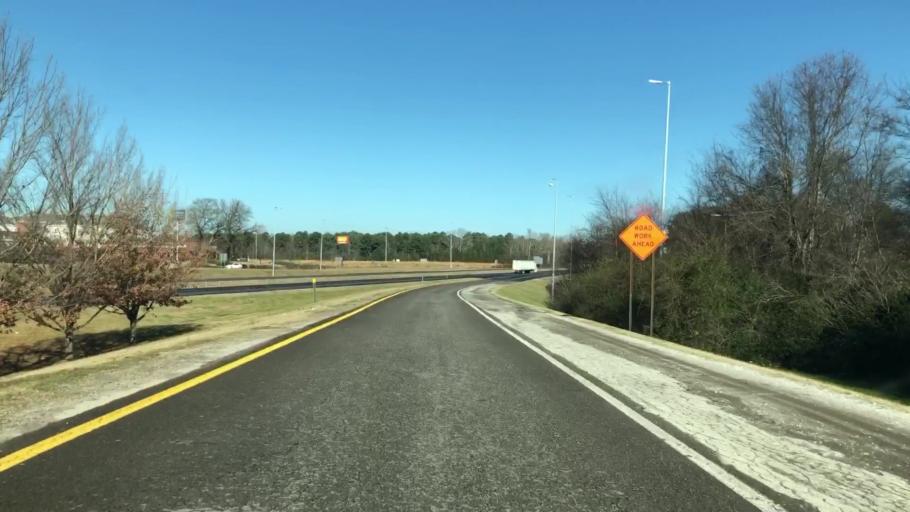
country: US
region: Alabama
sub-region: Limestone County
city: Athens
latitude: 34.7833
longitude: -86.9389
